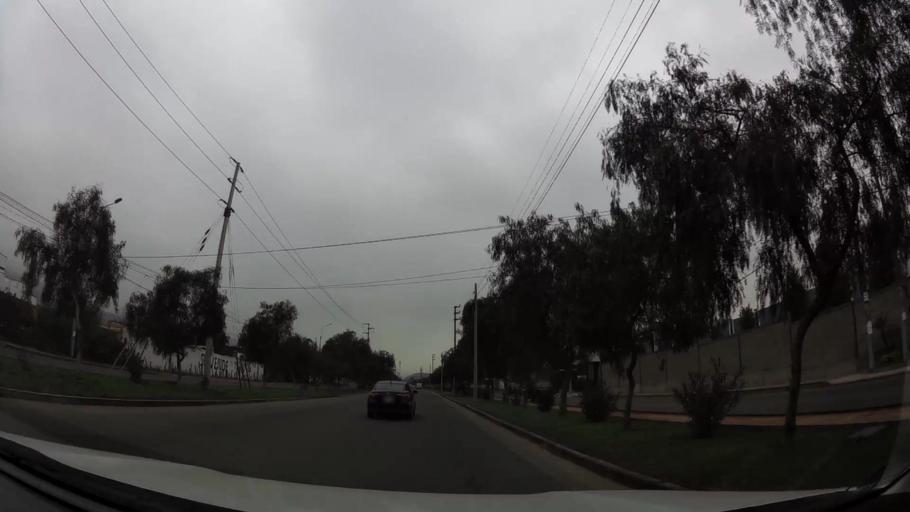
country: PE
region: Lima
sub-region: Lima
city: La Molina
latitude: -12.0863
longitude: -76.9056
